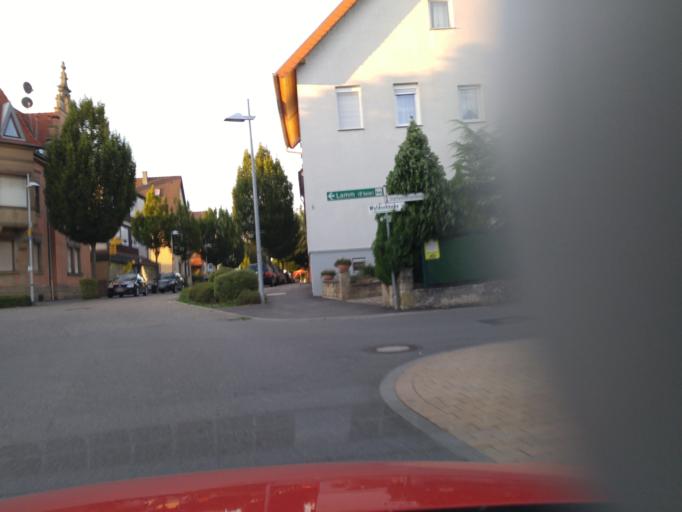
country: DE
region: Baden-Wuerttemberg
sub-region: Regierungsbezirk Stuttgart
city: Untereisesheim
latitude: 49.1962
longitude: 9.2020
